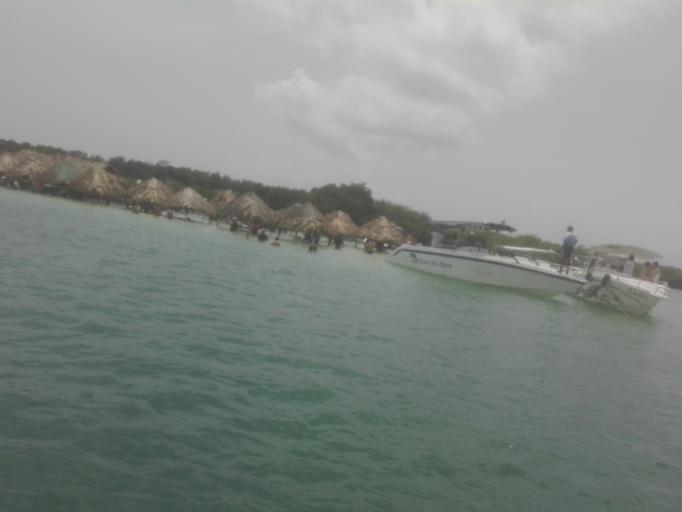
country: CO
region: Bolivar
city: Turbana
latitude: 10.1635
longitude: -75.6695
